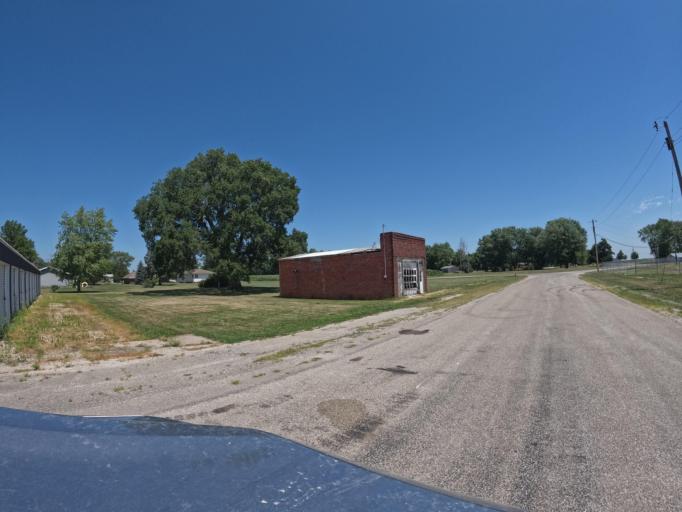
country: US
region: Iowa
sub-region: Keokuk County
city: Sigourney
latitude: 41.4555
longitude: -92.3331
